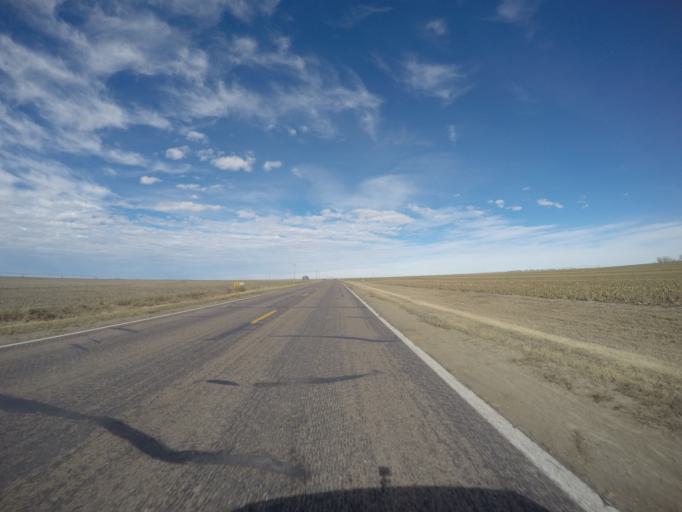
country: US
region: Nebraska
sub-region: Franklin County
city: Franklin
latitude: 40.2162
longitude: -98.9524
